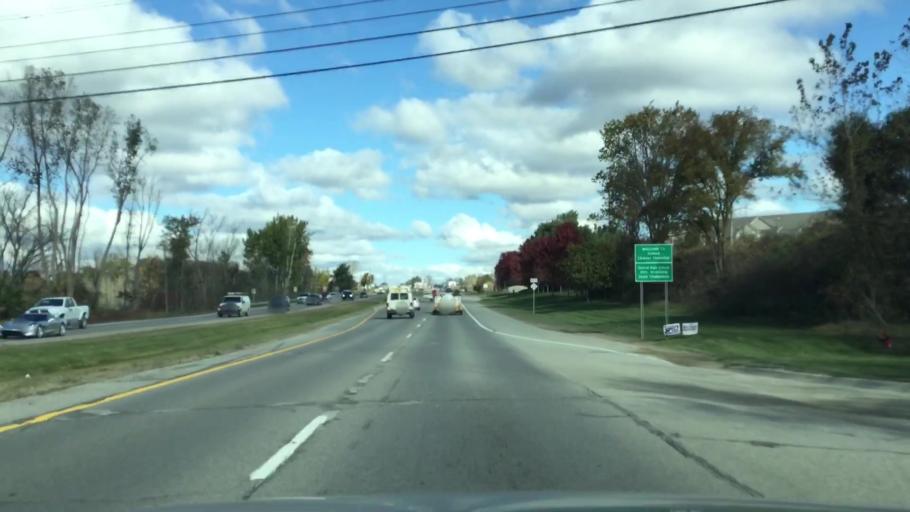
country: US
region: Michigan
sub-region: Oakland County
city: Lake Orion
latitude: 42.7974
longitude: -83.2468
